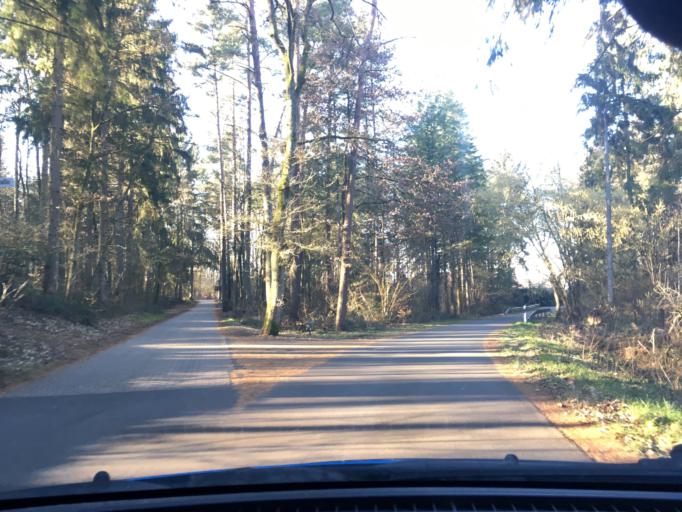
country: DE
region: Schleswig-Holstein
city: Schnakenbek
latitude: 53.3809
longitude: 10.5054
